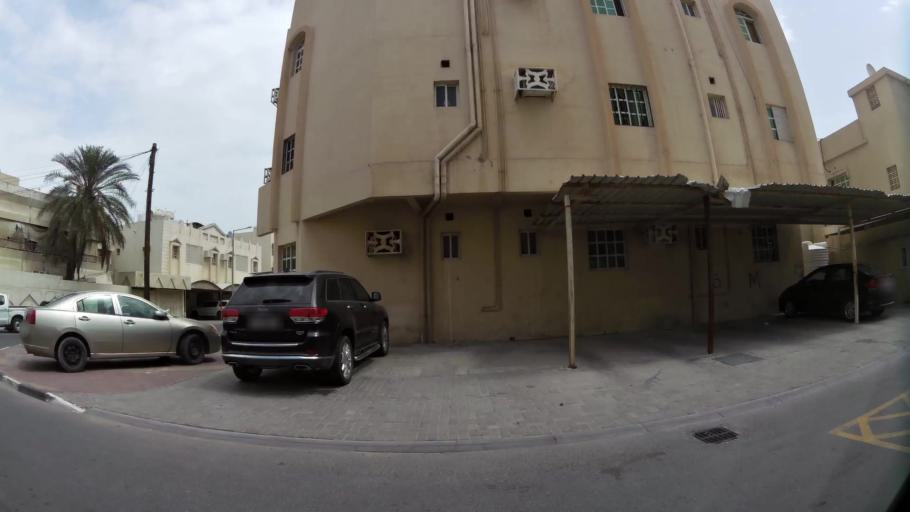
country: QA
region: Baladiyat ar Rayyan
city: Ar Rayyan
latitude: 25.3190
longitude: 51.4716
